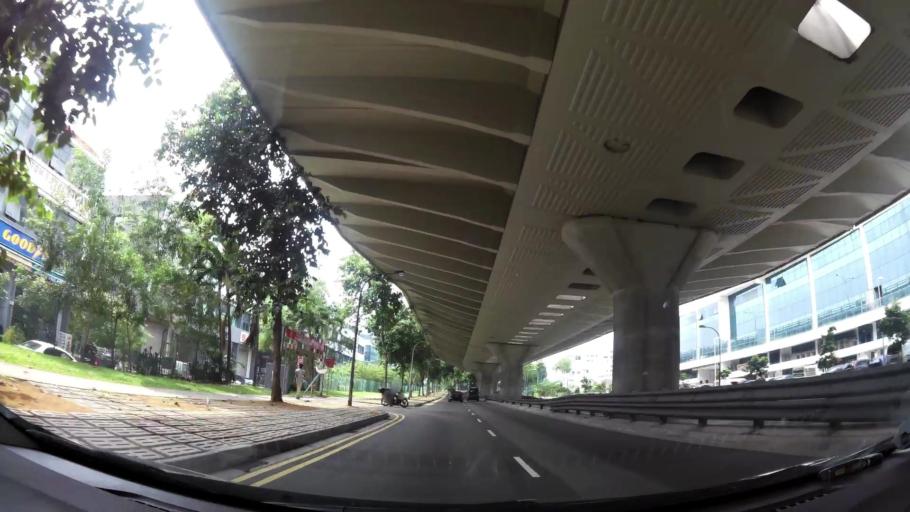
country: SG
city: Singapore
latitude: 1.3383
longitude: 103.9117
